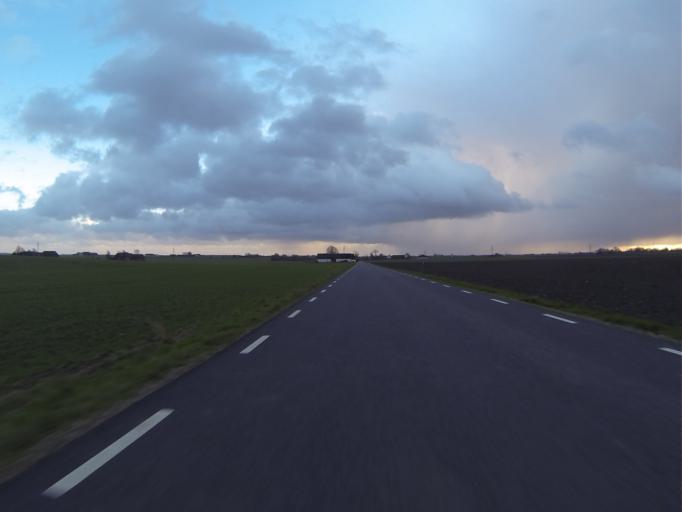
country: SE
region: Skane
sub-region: Lunds Kommun
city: Genarp
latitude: 55.6340
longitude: 13.3311
